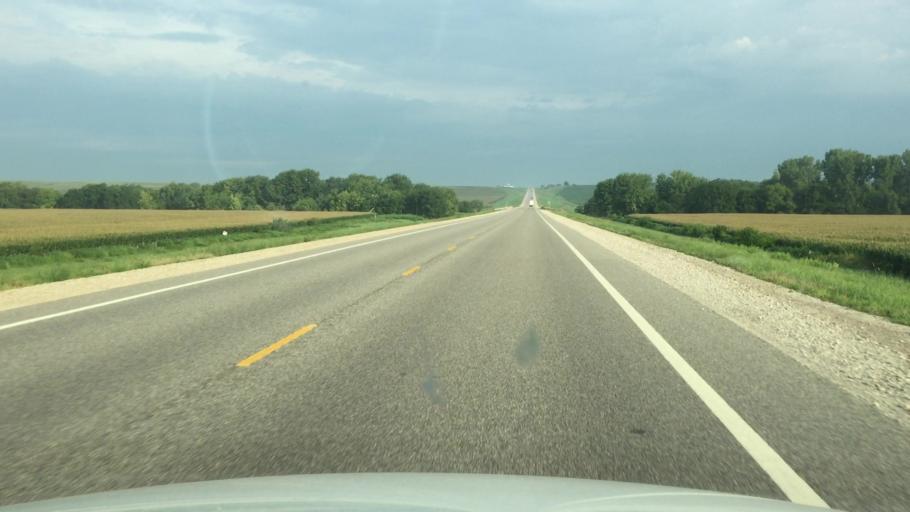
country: US
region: Kansas
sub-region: Doniphan County
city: Highland
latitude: 39.8137
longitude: -95.1992
